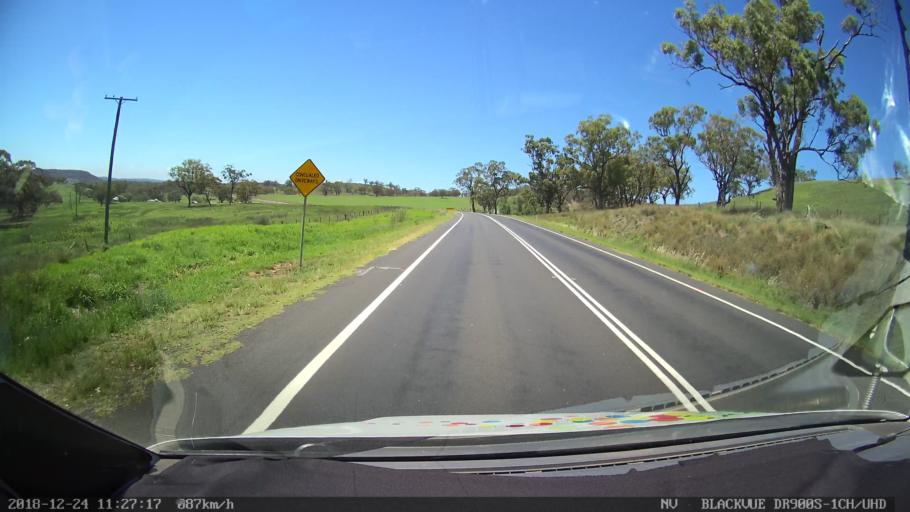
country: AU
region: New South Wales
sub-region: Upper Hunter Shire
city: Merriwa
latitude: -32.1802
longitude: 150.4345
